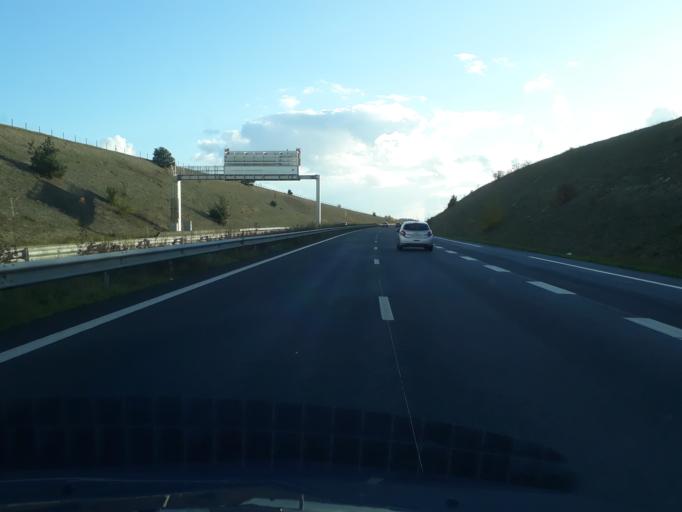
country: FR
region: Champagne-Ardenne
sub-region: Departement de la Marne
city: Fagnieres
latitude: 48.9472
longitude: 4.2896
